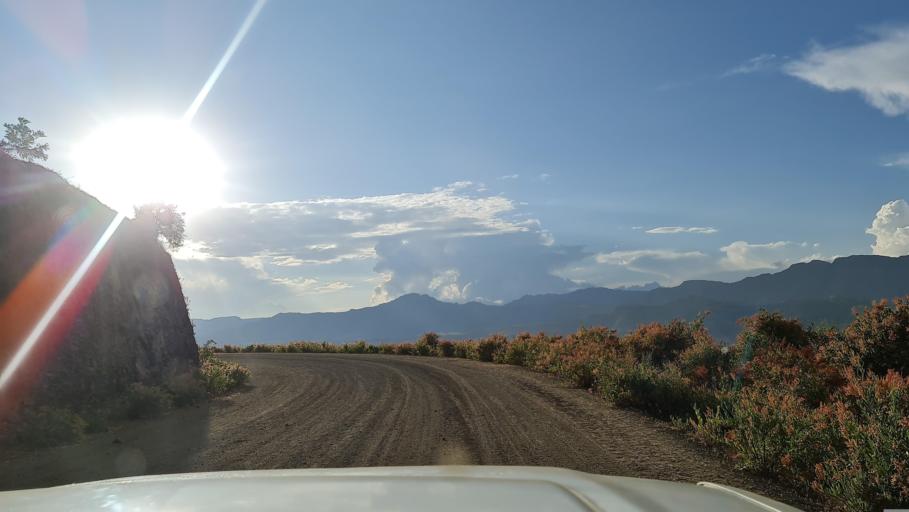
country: ET
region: Amhara
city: Debark'
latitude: 13.0482
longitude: 38.0211
